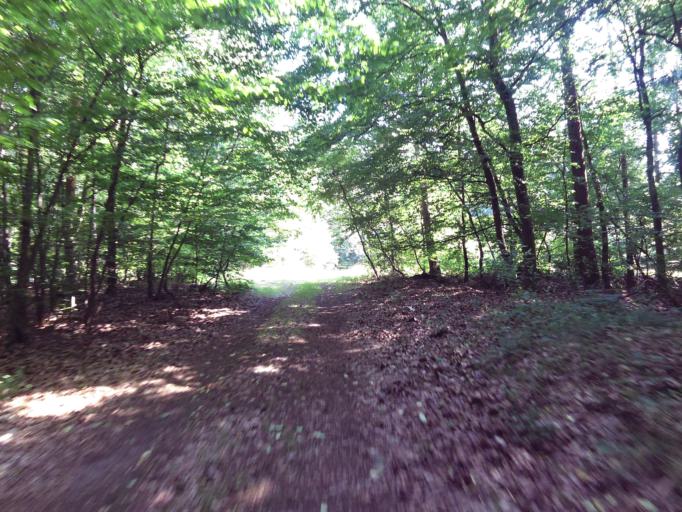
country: DE
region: Hesse
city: Morfelden-Walldorf
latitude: 50.0033
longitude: 8.6062
